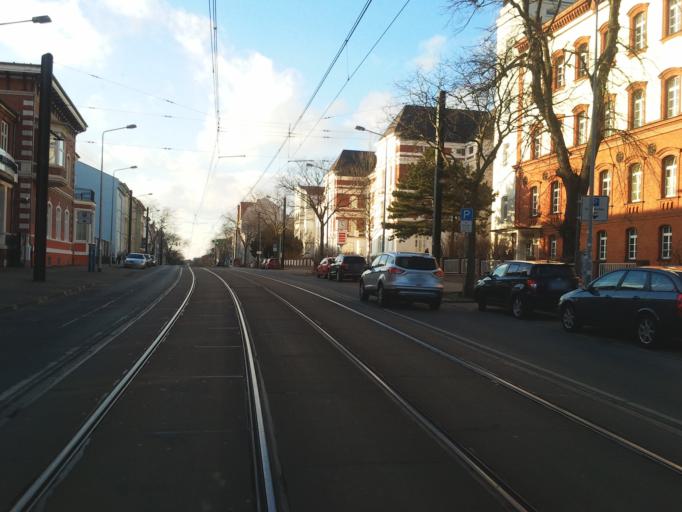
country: DE
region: Mecklenburg-Vorpommern
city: Rostock
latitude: 54.0896
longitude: 12.1199
